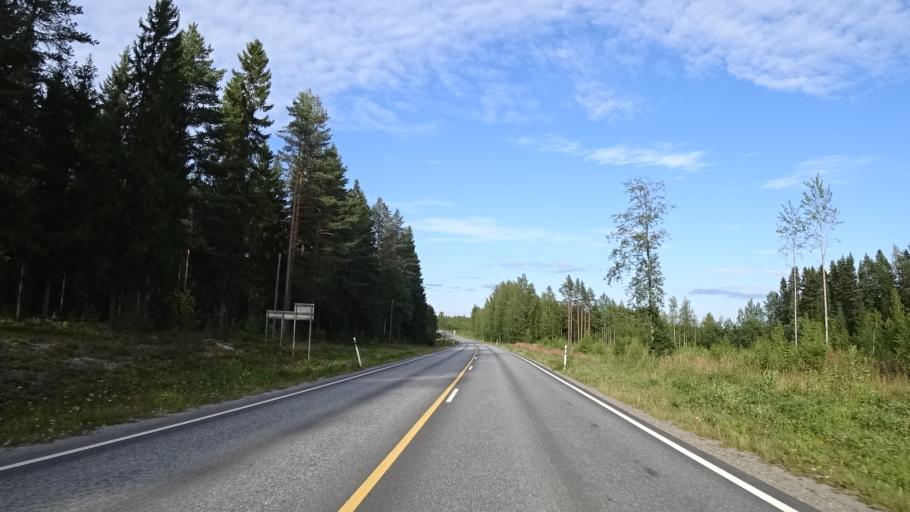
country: FI
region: North Karelia
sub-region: Joensuu
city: Eno
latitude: 62.8101
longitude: 30.1628
